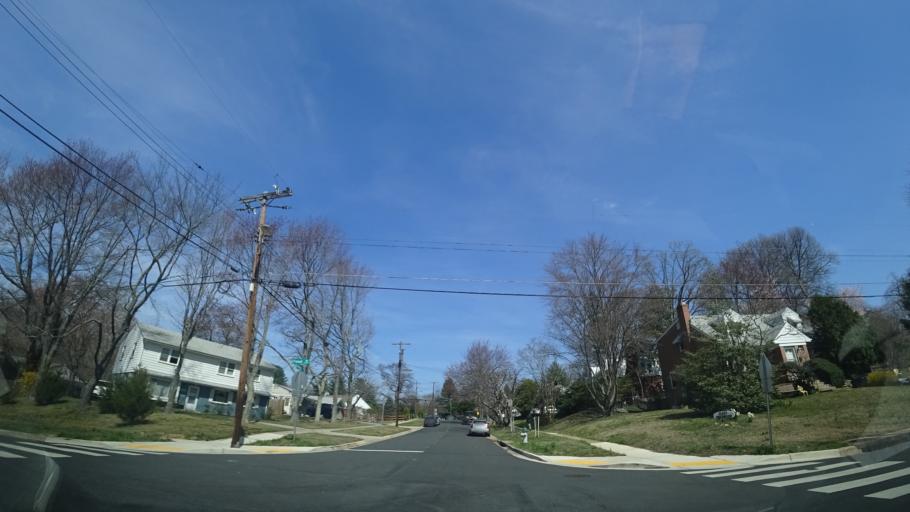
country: US
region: Maryland
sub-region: Montgomery County
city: Glenmont
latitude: 39.0460
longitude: -77.0365
